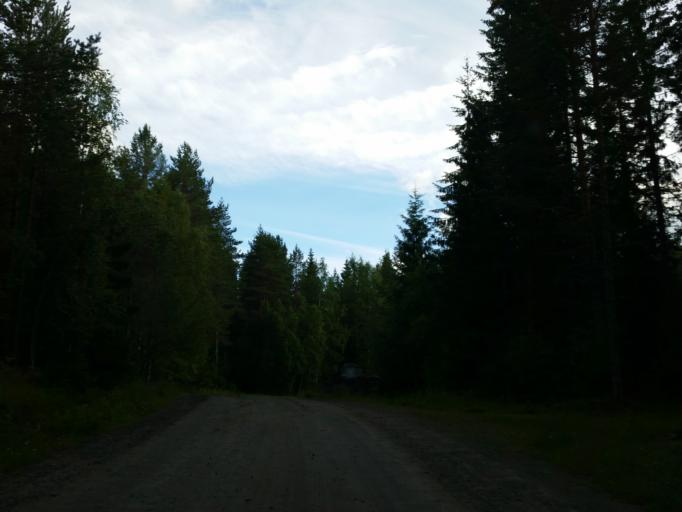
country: SE
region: Vaesterbotten
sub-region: Robertsfors Kommun
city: Robertsfors
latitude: 64.0454
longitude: 20.8507
